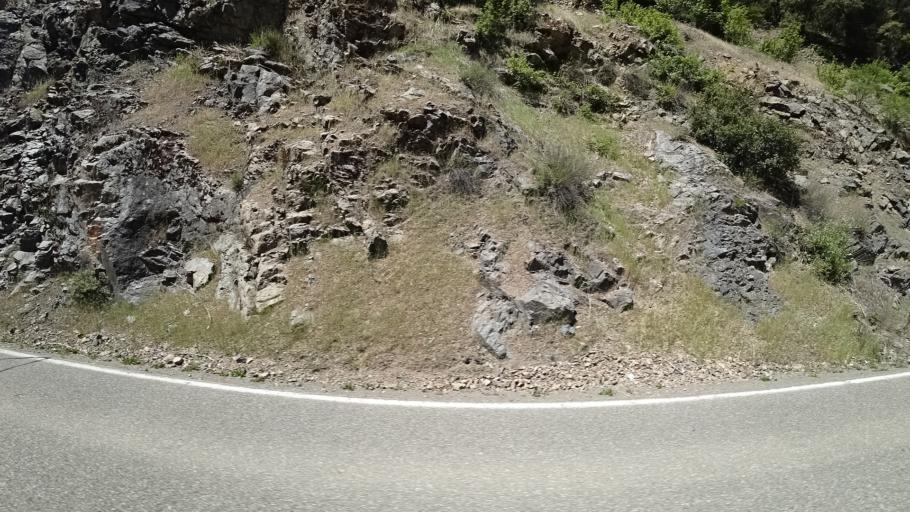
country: US
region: California
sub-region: Trinity County
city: Hayfork
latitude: 40.7670
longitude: -123.2994
